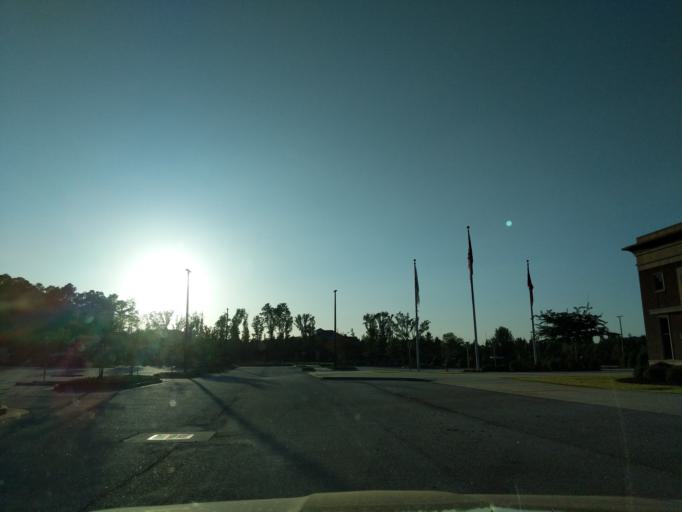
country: US
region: Georgia
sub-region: Columbia County
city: Grovetown
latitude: 33.4779
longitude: -82.1901
